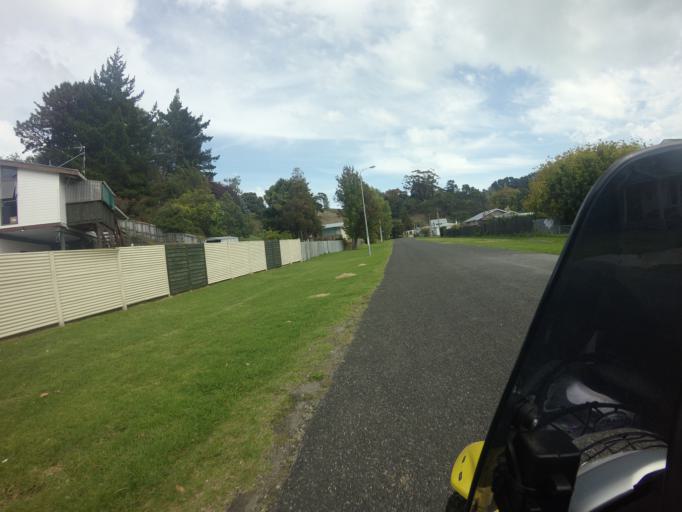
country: NZ
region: Gisborne
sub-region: Gisborne District
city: Gisborne
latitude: -38.6778
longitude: 178.0439
